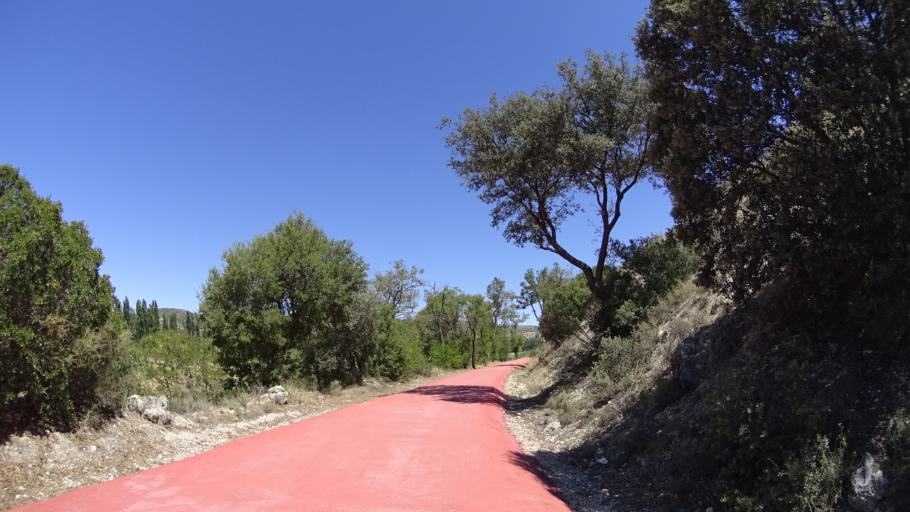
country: ES
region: Madrid
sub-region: Provincia de Madrid
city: Ambite
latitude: 40.3105
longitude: -3.1914
